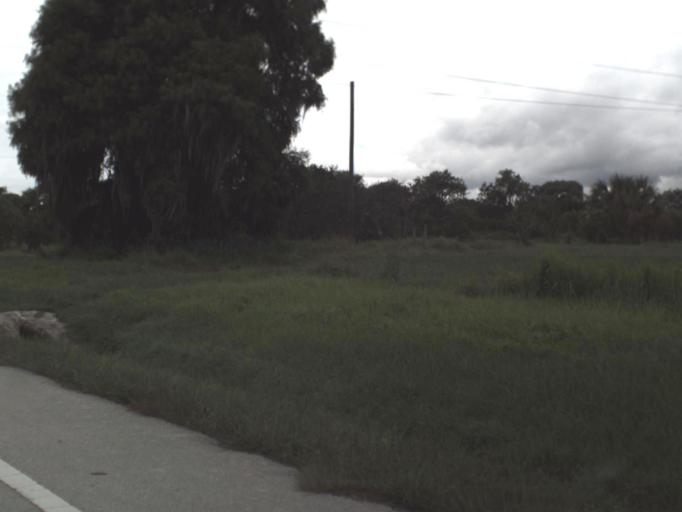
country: US
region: Florida
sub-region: Hardee County
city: Bowling Green
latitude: 27.5949
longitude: -81.8286
